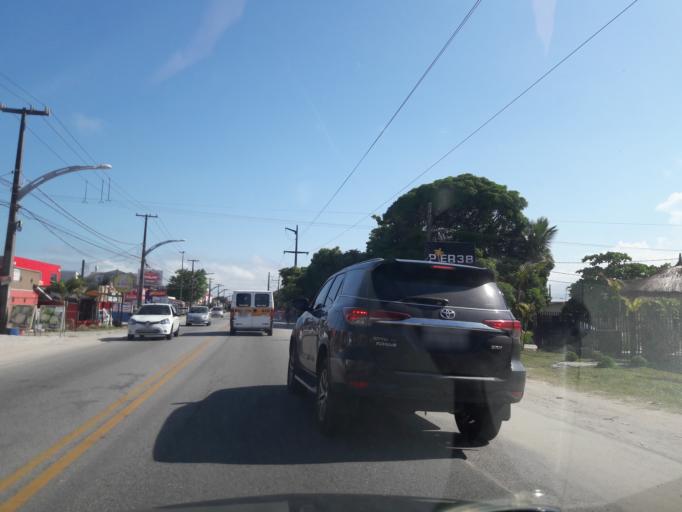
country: BR
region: Parana
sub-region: Pontal Do Parana
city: Pontal do Parana
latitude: -25.6900
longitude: -48.4721
